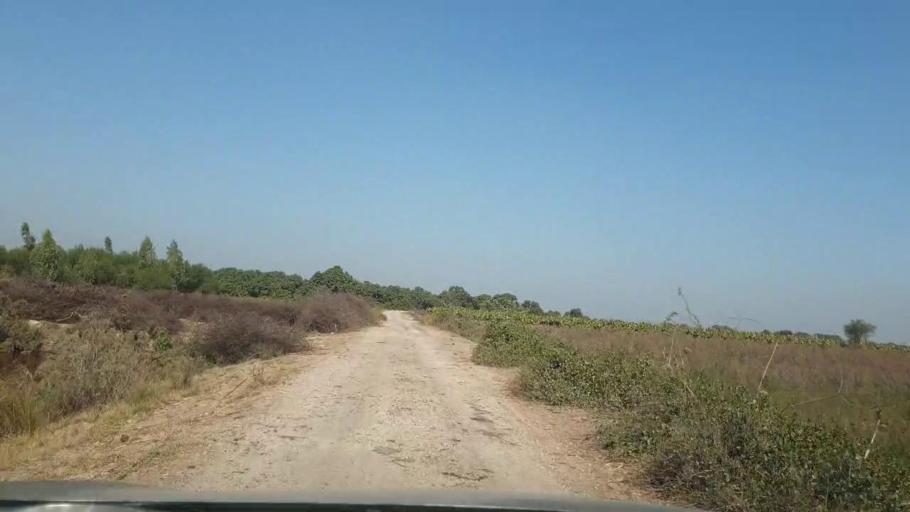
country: PK
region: Sindh
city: Tando Adam
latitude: 25.6195
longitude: 68.6462
